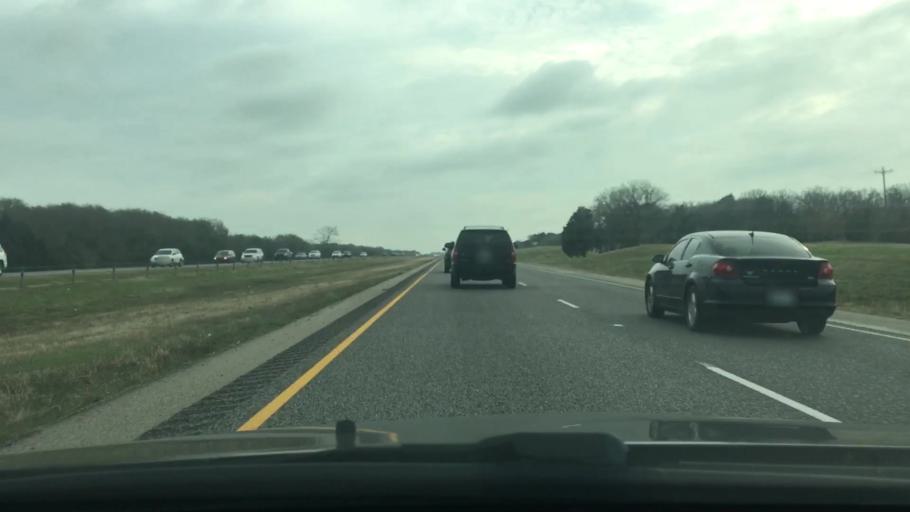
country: US
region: Texas
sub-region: Freestone County
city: Fairfield
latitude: 31.6235
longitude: -96.1576
